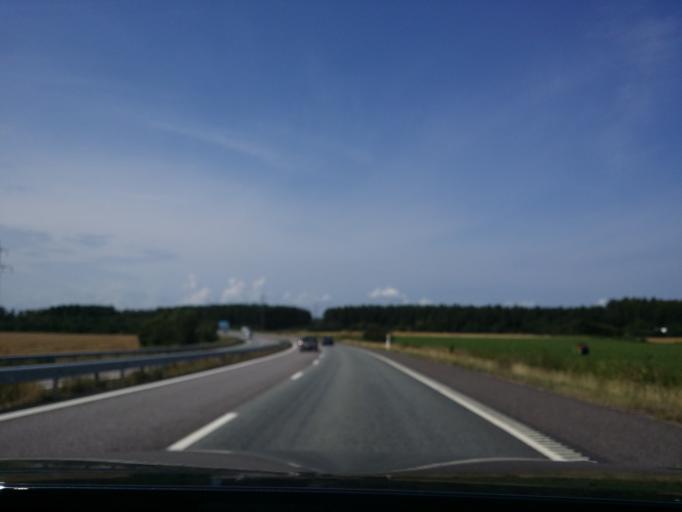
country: SE
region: Blekinge
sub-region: Solvesborgs Kommun
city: Soelvesborg
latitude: 56.0708
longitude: 14.5351
